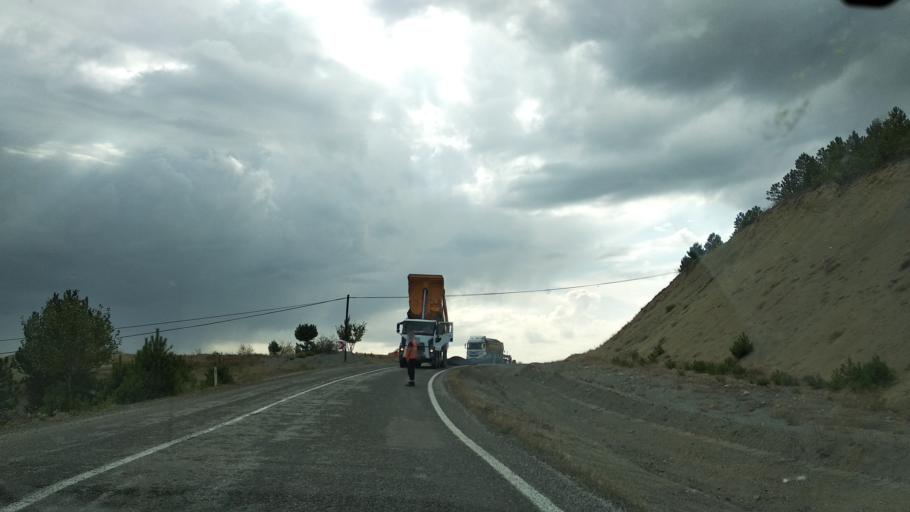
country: TR
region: Bolu
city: Seben
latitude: 40.3552
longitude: 31.4832
